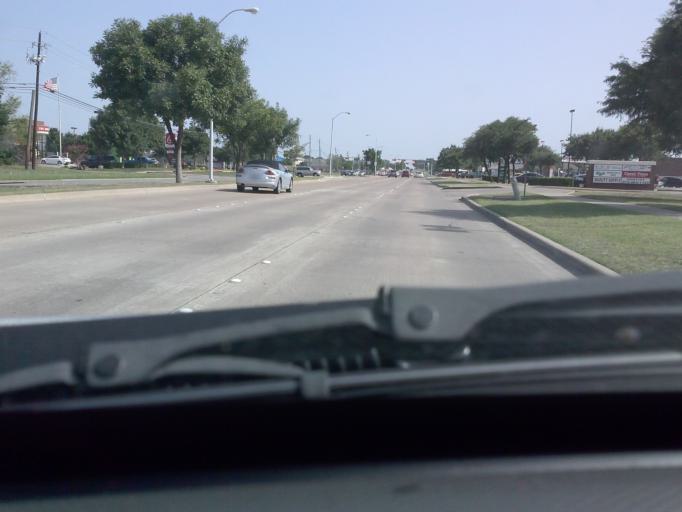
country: US
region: Texas
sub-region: Collin County
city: Plano
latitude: 33.0589
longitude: -96.7706
